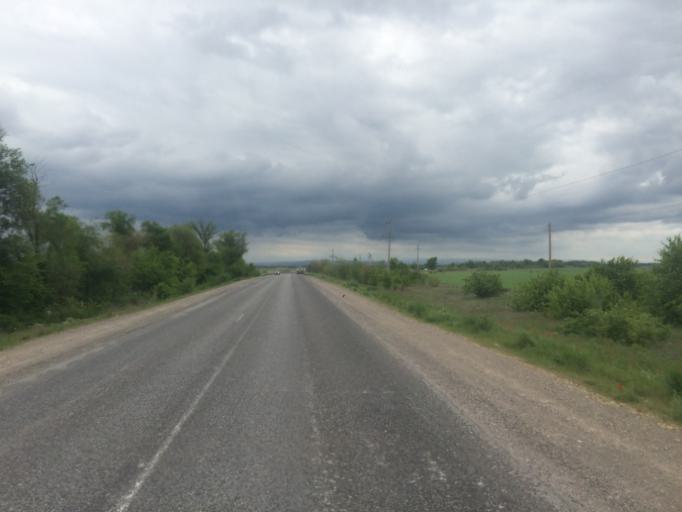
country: KZ
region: Zhambyl
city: Georgiyevka
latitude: 43.2042
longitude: 74.5072
